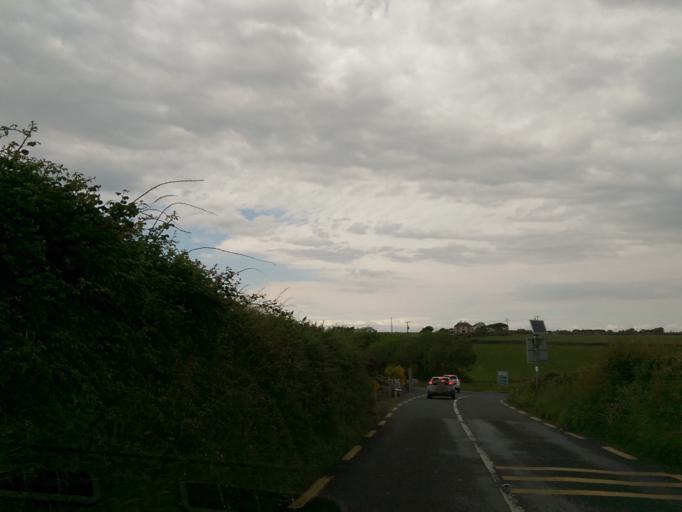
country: IE
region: Connaught
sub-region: County Galway
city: Bearna
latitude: 53.1462
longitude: -9.0798
